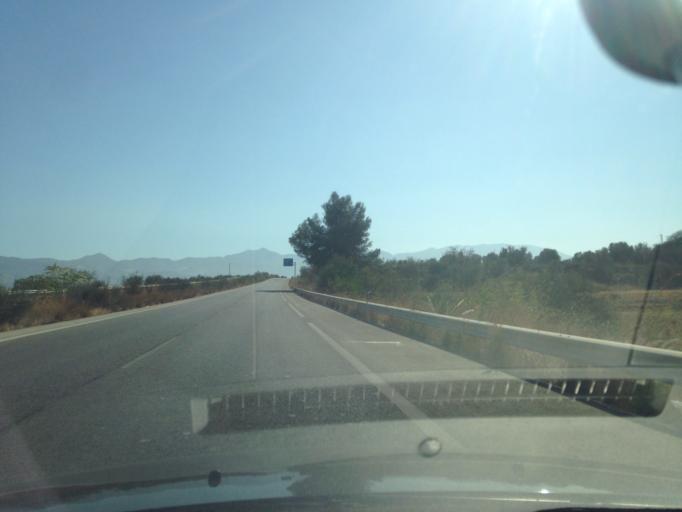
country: ES
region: Andalusia
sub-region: Provincia de Malaga
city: Alhaurin de la Torre
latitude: 36.7256
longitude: -4.5525
